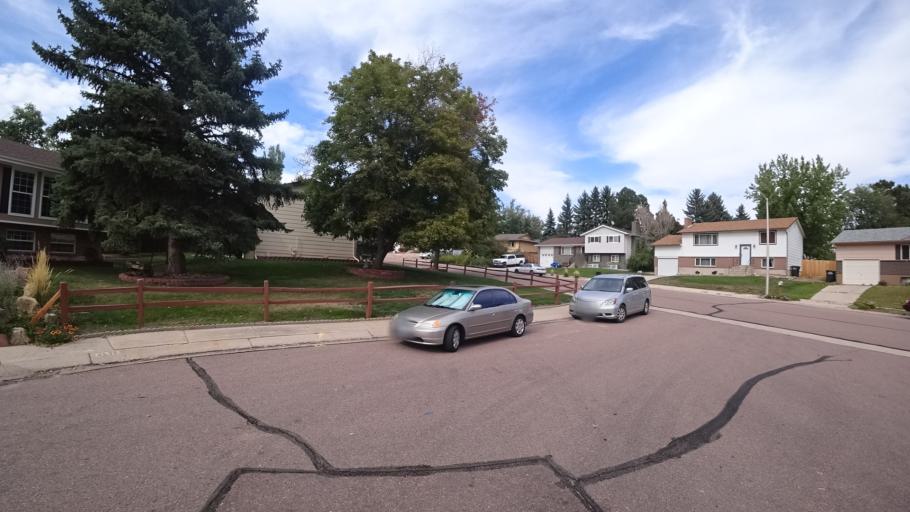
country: US
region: Colorado
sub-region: El Paso County
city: Colorado Springs
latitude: 38.9011
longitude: -104.7718
